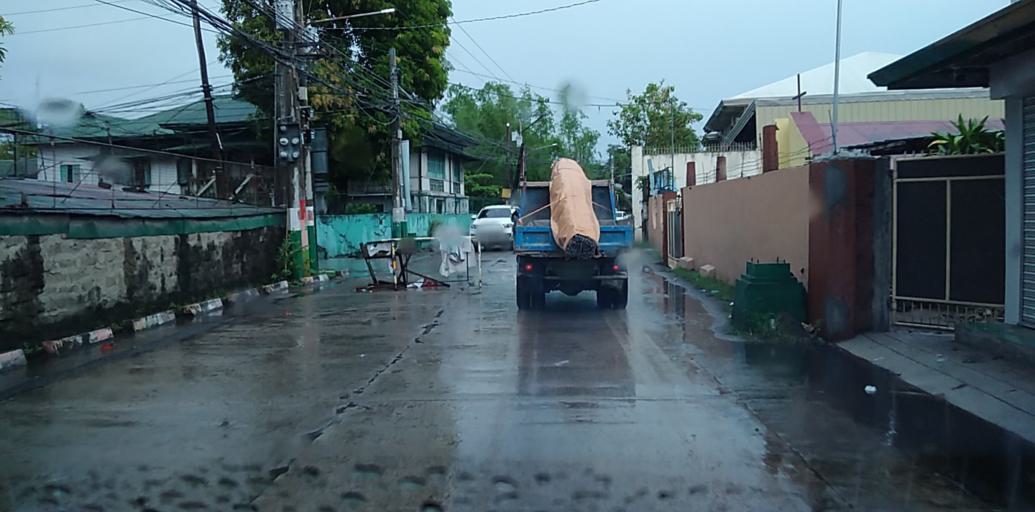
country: PH
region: Central Luzon
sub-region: Province of Pampanga
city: Mexico
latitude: 15.0669
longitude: 120.7209
